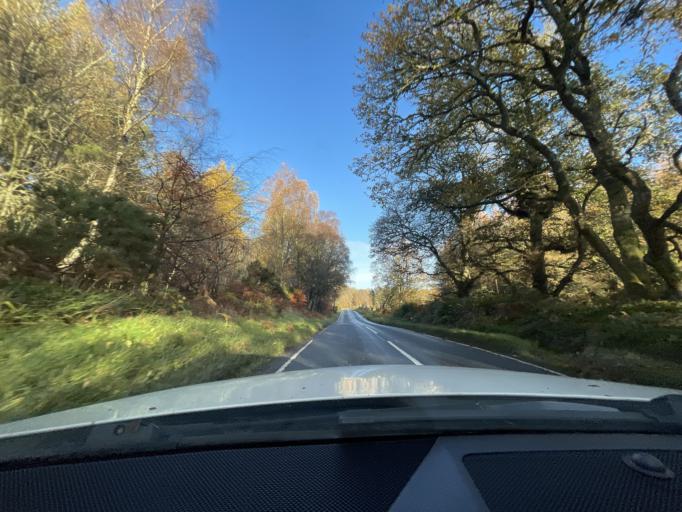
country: GB
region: Scotland
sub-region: Highland
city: Inverness
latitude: 57.4203
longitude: -4.2974
